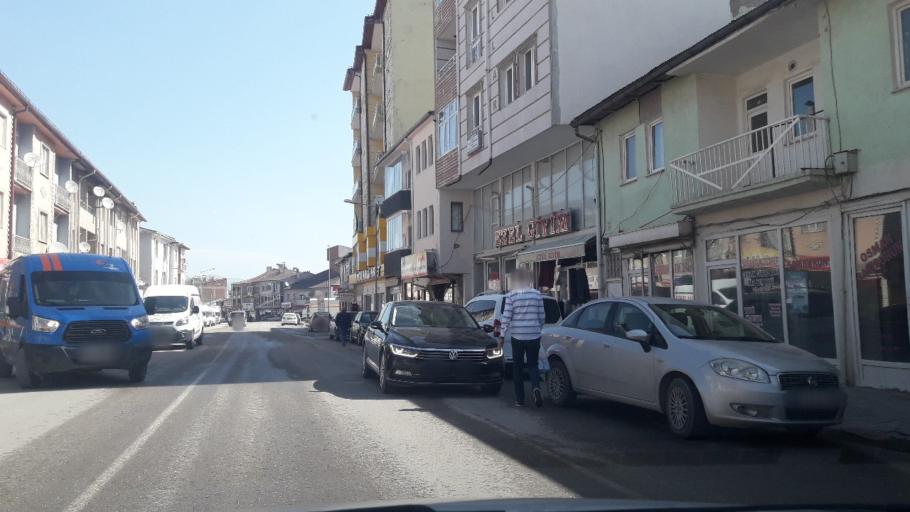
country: TR
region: Sivas
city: Kangal
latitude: 39.2333
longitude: 37.3904
